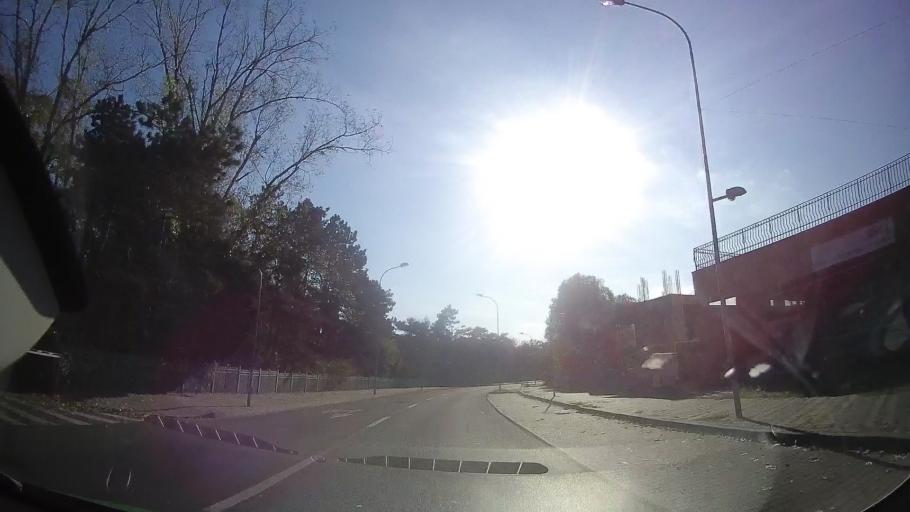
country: RO
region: Constanta
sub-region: Comuna Douazeci si Trei August
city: Douazeci si Trei August
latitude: 43.8750
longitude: 28.6029
